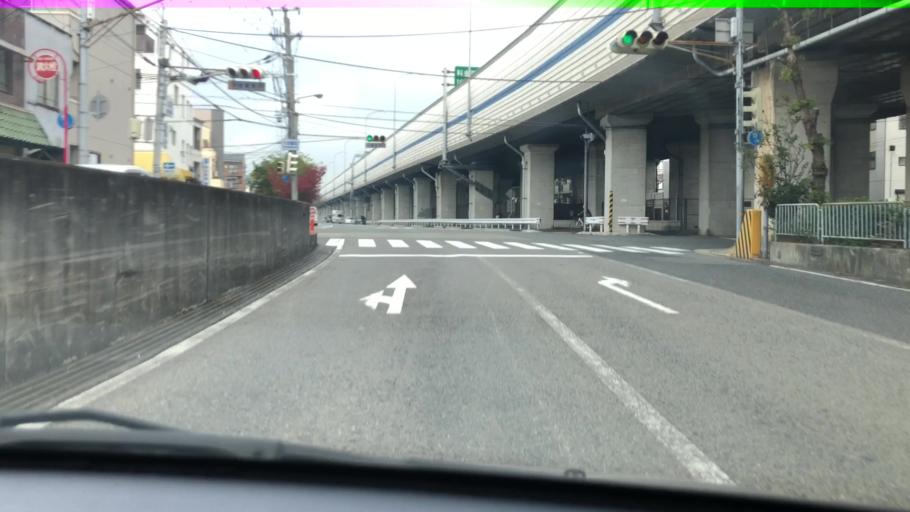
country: JP
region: Hyogo
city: Nishinomiya-hama
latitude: 34.7286
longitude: 135.3572
